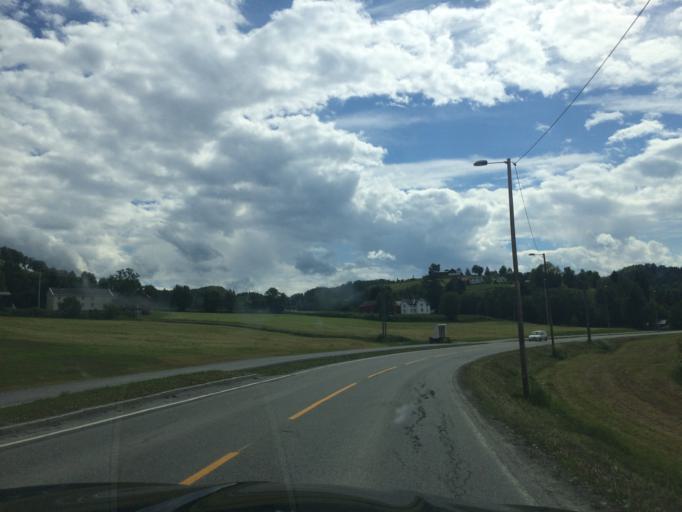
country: NO
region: Sor-Trondelag
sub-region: Selbu
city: Mebonden
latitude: 63.2457
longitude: 11.0910
